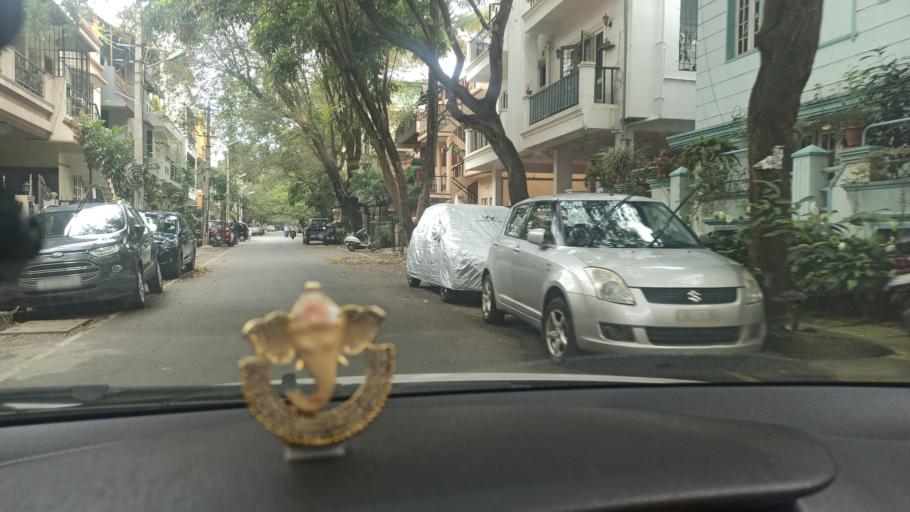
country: IN
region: Karnataka
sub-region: Bangalore Urban
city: Bangalore
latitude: 12.9186
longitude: 77.6316
